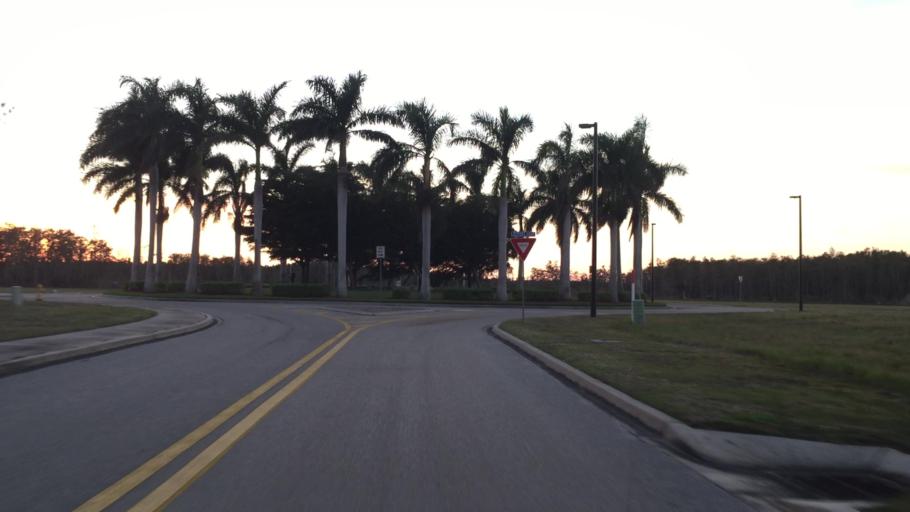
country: US
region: Florida
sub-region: Lee County
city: Three Oaks
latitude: 26.5296
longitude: -81.7897
